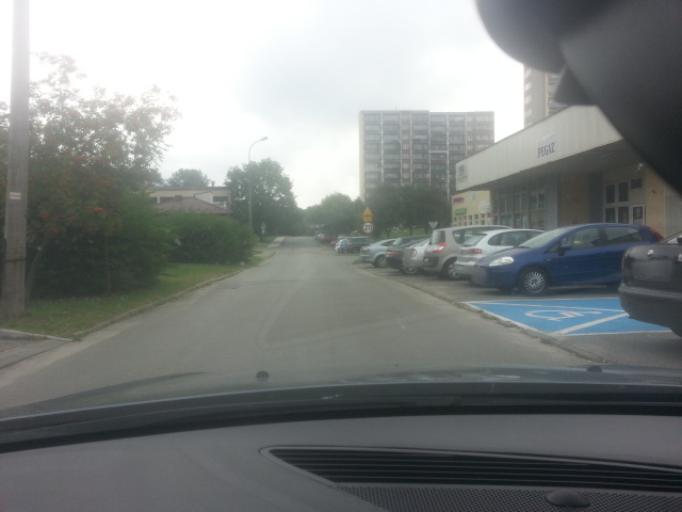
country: PL
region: Lesser Poland Voivodeship
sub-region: Powiat chrzanowski
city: Chrzanow
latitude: 50.1432
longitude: 19.4176
